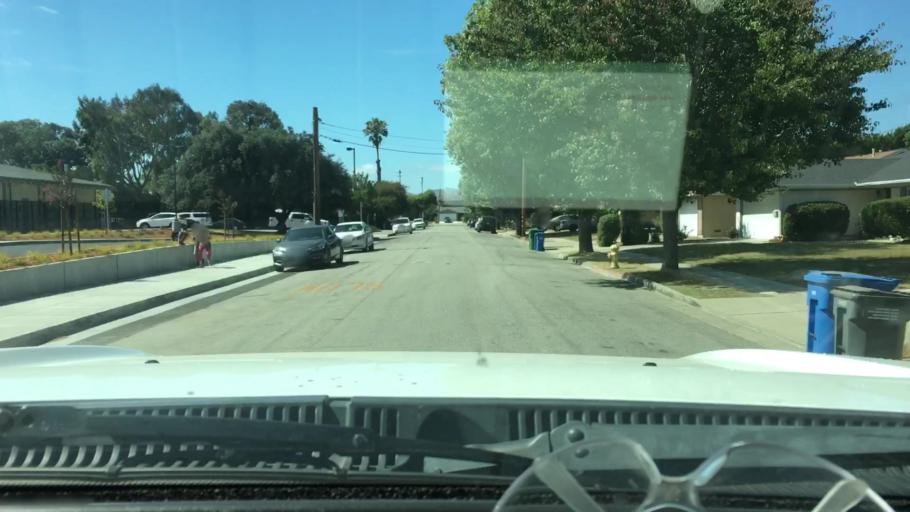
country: US
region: California
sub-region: San Luis Obispo County
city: San Luis Obispo
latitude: 35.2620
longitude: -120.6884
